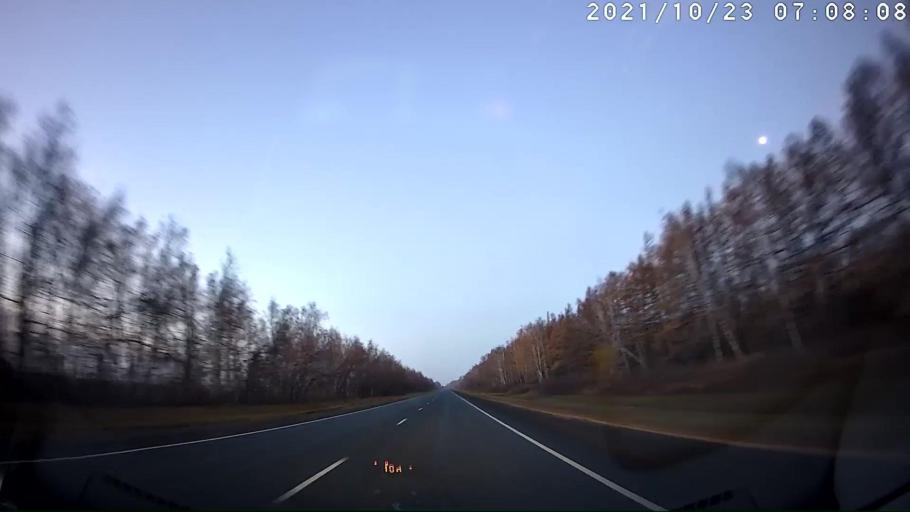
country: RU
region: Saratov
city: Khvalynsk
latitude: 52.5736
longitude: 48.1063
